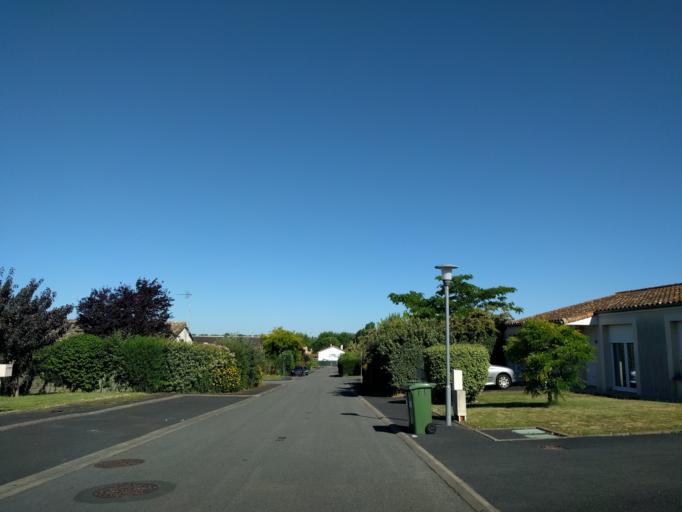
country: FR
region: Poitou-Charentes
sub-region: Departement des Deux-Sevres
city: Niort
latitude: 46.3420
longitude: -0.4476
